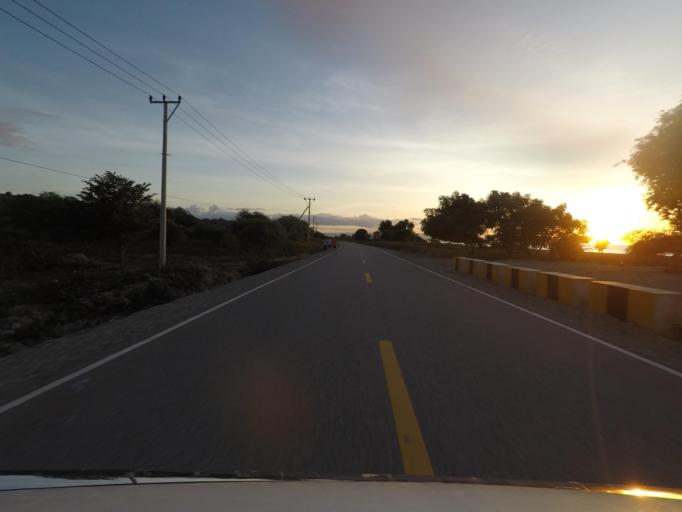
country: TL
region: Baucau
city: Baucau
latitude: -8.4561
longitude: 126.6212
